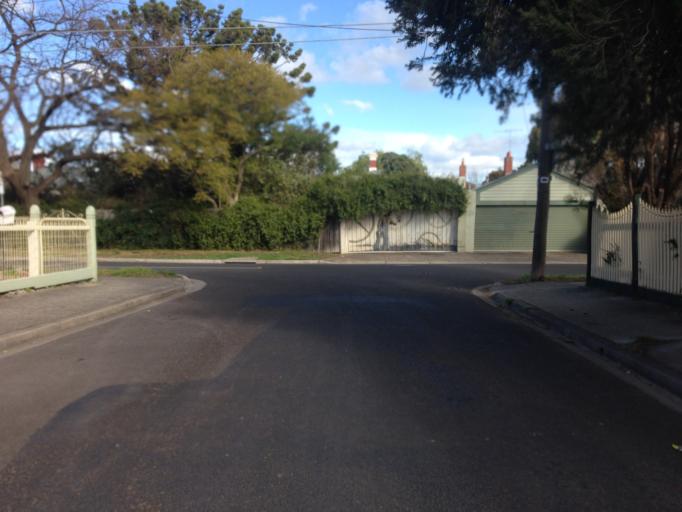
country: AU
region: Victoria
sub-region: Darebin
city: Fairfield
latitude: -37.7783
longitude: 145.0055
